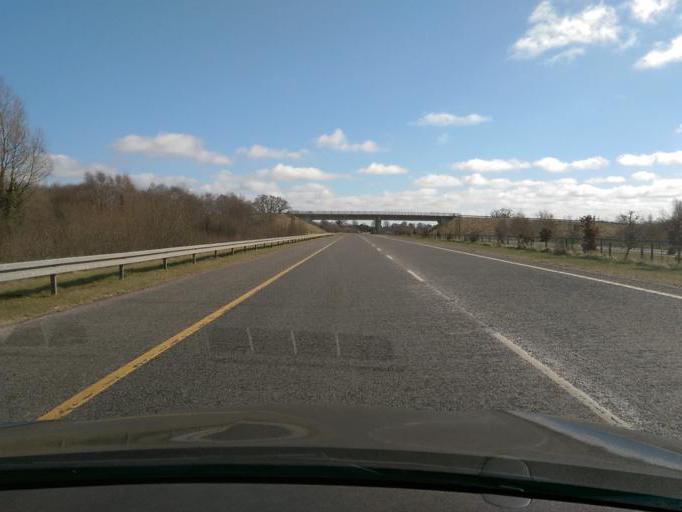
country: IE
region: Leinster
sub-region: An Mhi
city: Longwood
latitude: 53.4261
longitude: -6.9308
